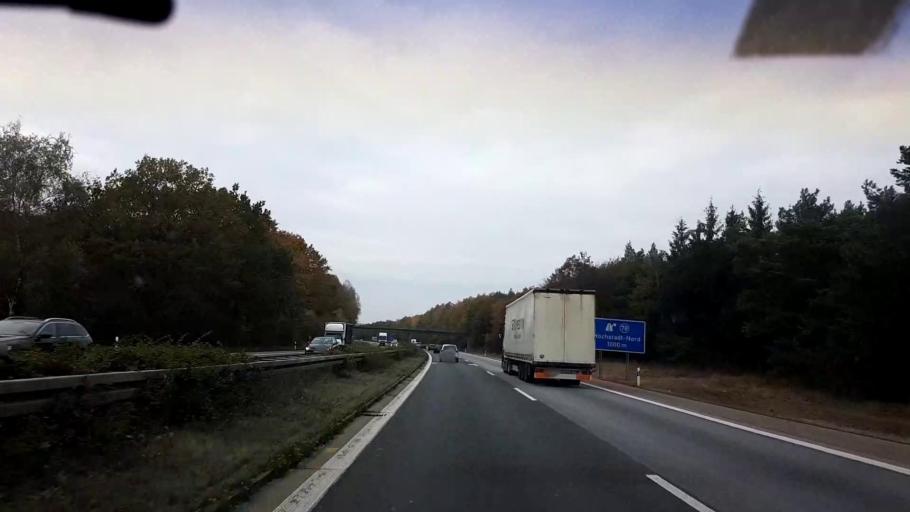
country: DE
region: Bavaria
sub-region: Regierungsbezirk Mittelfranken
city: Hochstadt an der Aisch
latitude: 49.7349
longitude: 10.8090
